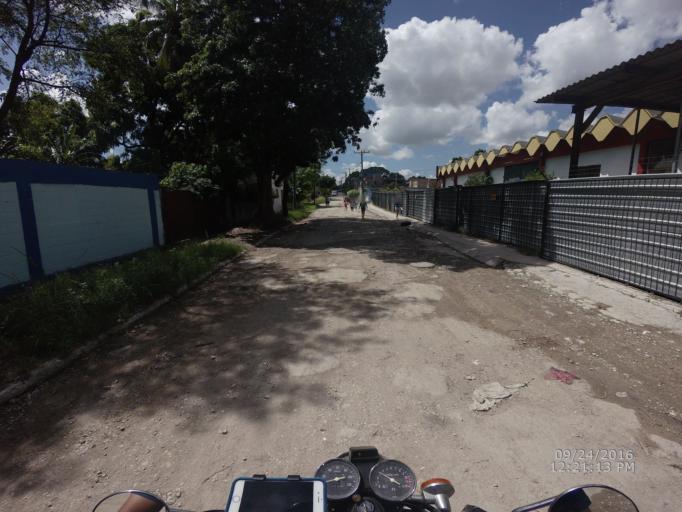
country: CU
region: La Habana
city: Diez de Octubre
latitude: 23.0954
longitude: -82.3558
